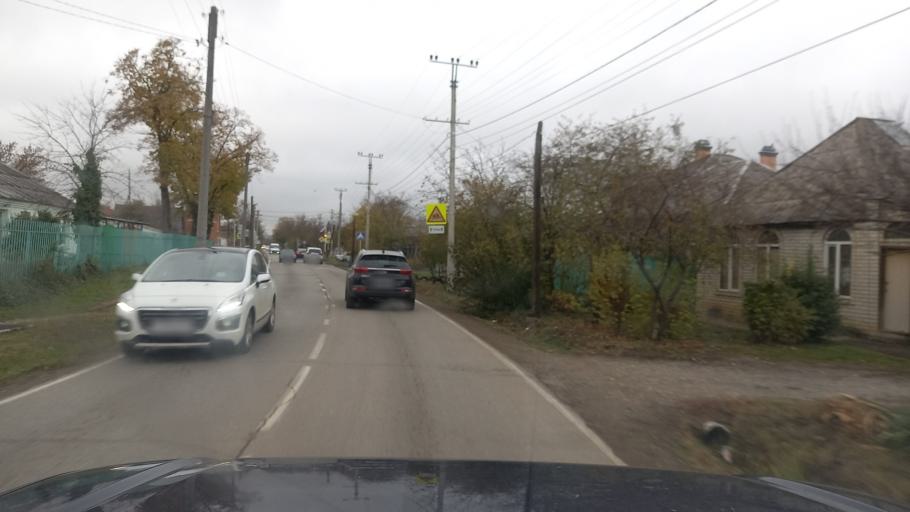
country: RU
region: Adygeya
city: Maykop
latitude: 44.6063
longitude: 40.0877
